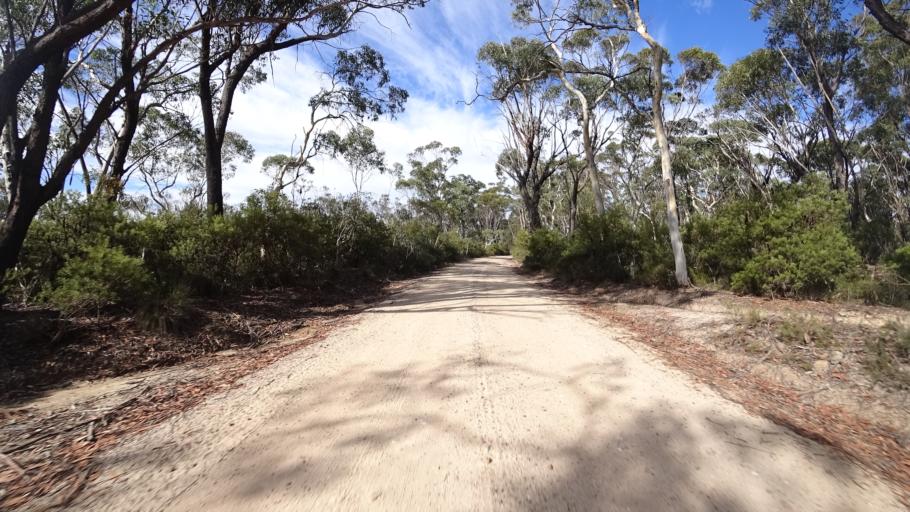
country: AU
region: New South Wales
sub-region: Lithgow
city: Lithgow
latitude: -33.4979
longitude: 150.1661
